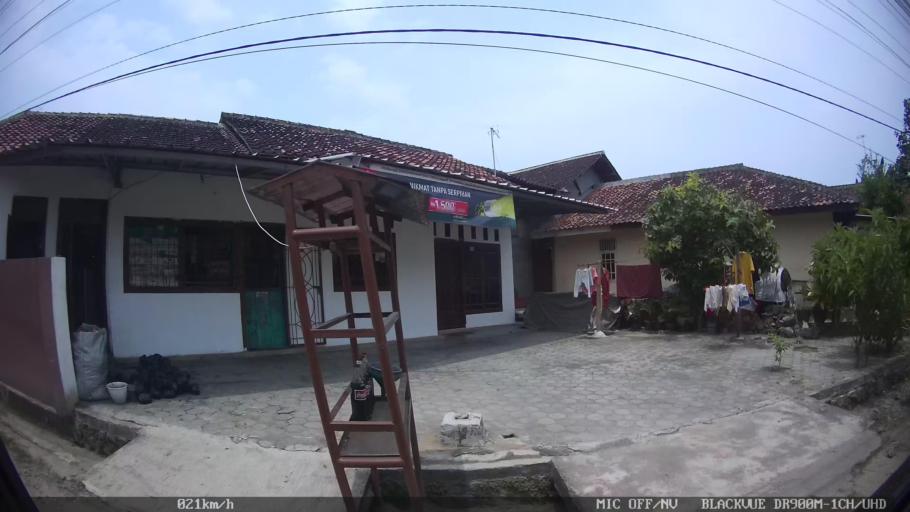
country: ID
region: Lampung
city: Kedaton
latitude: -5.3937
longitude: 105.3023
